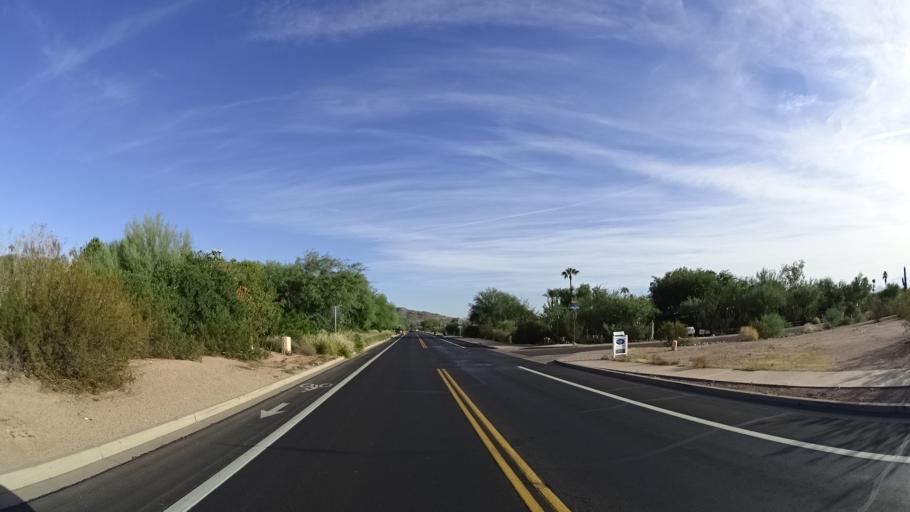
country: US
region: Arizona
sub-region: Maricopa County
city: Paradise Valley
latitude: 33.5182
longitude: -111.9433
